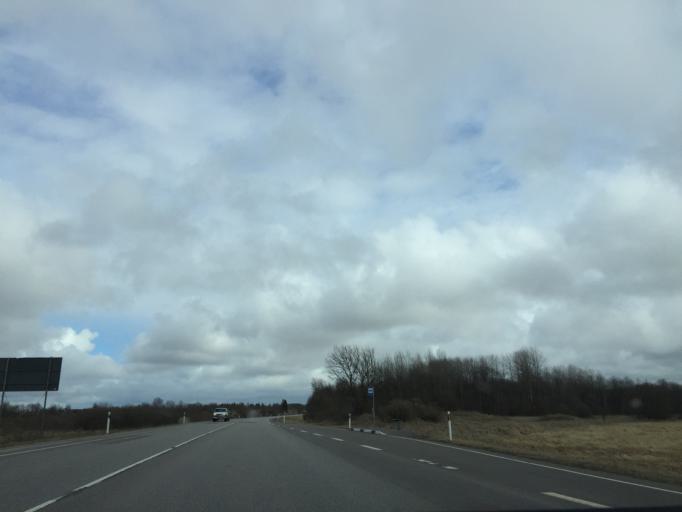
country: EE
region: Laeaene
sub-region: Lihula vald
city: Lihula
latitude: 58.7242
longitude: 23.9177
